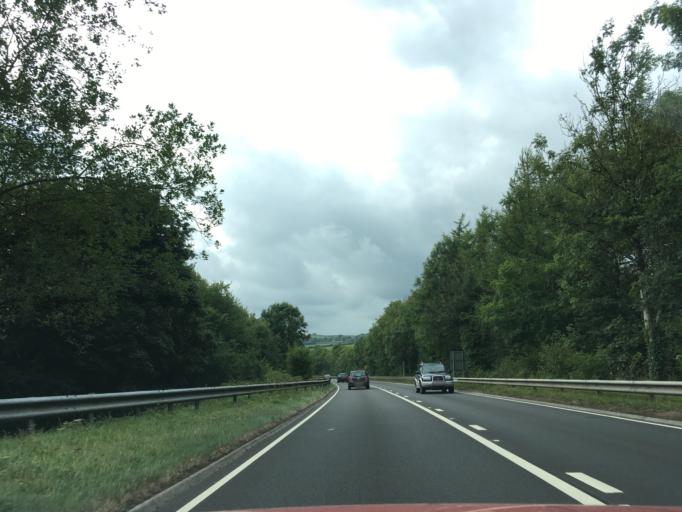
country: GB
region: Wales
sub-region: Carmarthenshire
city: Llanddowror
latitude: 51.8261
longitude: -4.5542
